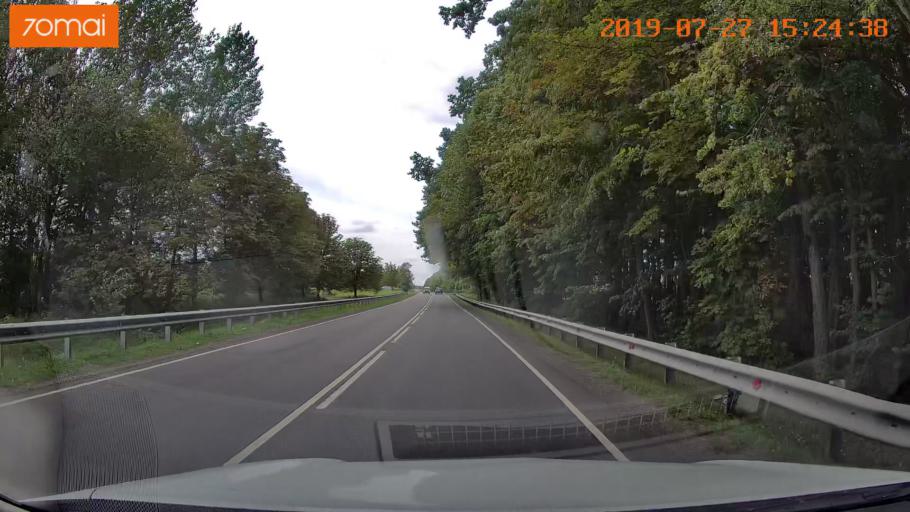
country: RU
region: Kaliningrad
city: Nesterov
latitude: 54.6358
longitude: 22.6064
